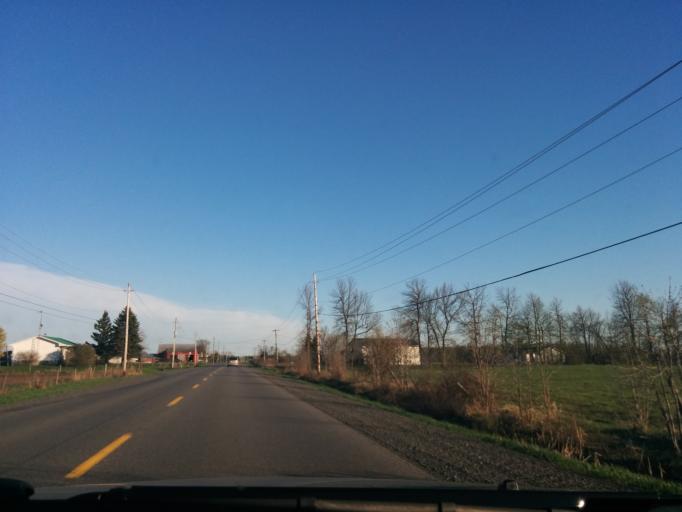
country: CA
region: Ontario
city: Bells Corners
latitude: 45.1576
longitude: -75.6243
